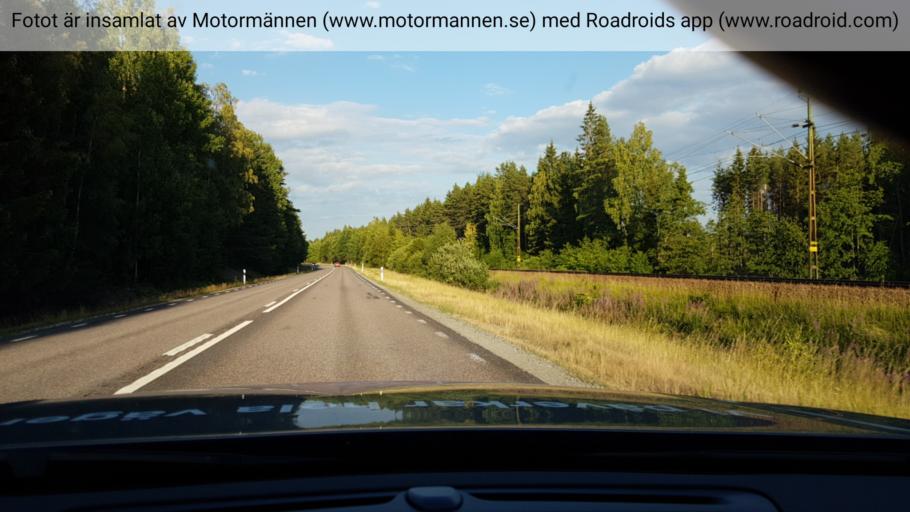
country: SE
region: Uppsala
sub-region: Enkopings Kommun
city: Orsundsbro
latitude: 59.8813
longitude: 17.2341
